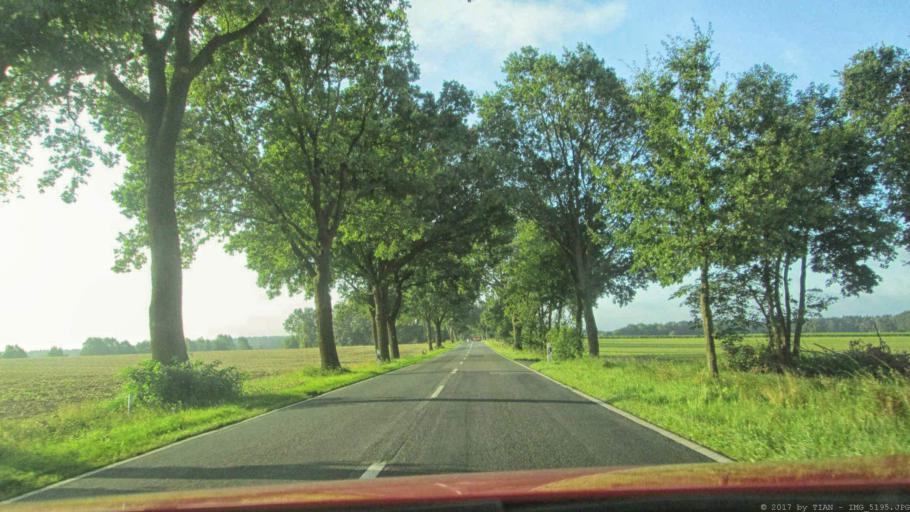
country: DE
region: Lower Saxony
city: Wieren
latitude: 52.8783
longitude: 10.6657
